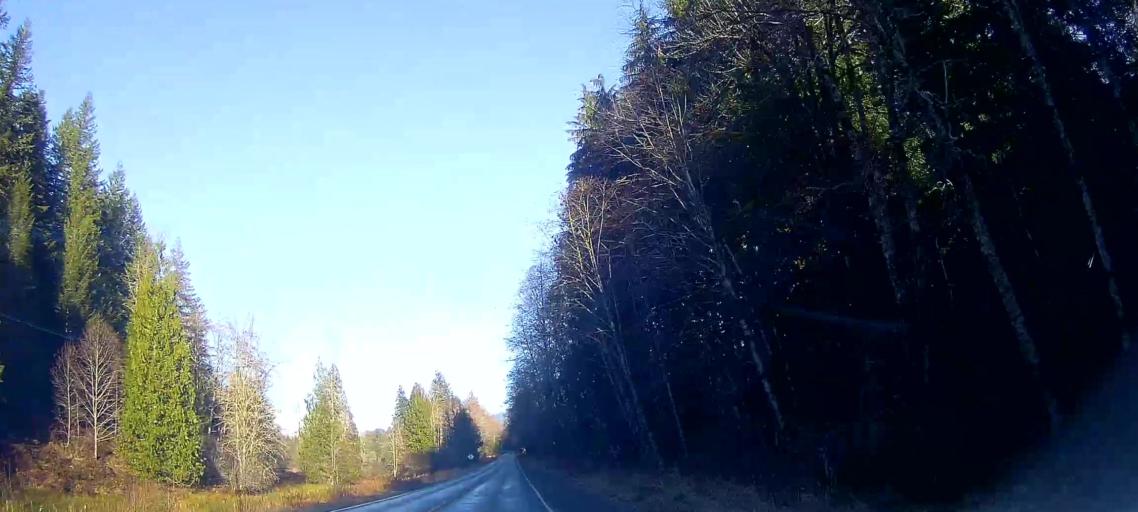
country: US
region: Washington
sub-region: Snohomish County
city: Darrington
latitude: 48.6018
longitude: -121.7642
